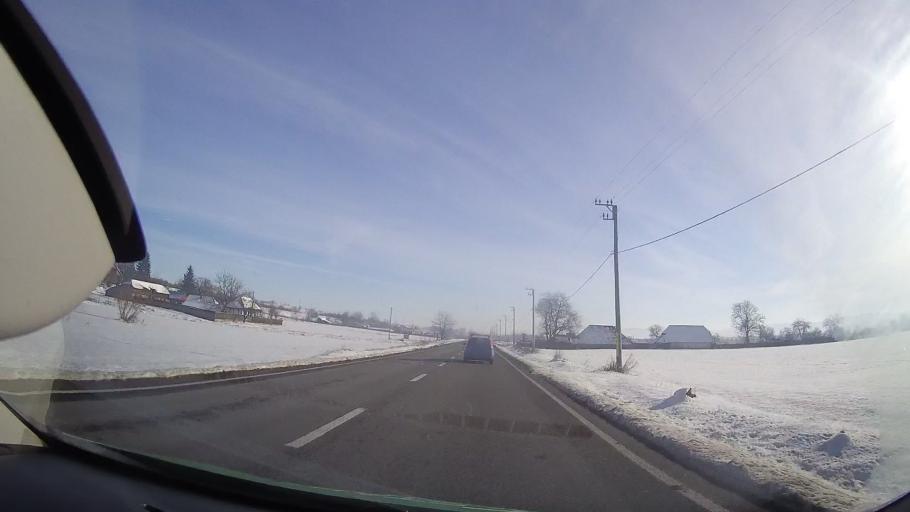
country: RO
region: Neamt
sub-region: Comuna Ghindaoani
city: Ghindaoani
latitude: 47.0798
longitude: 26.3462
